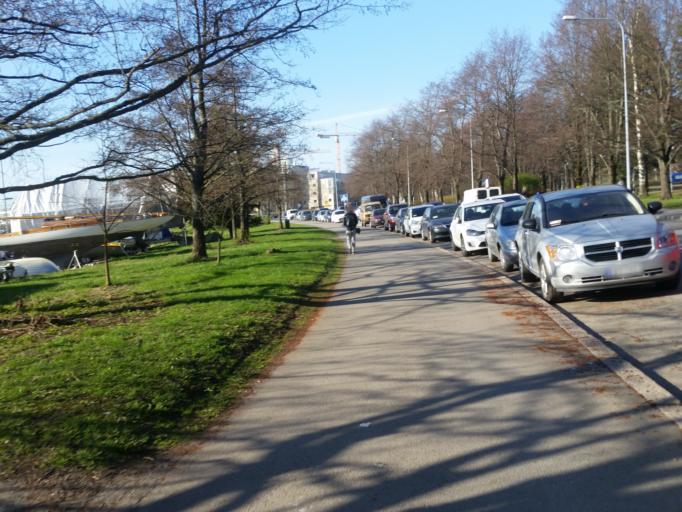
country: FI
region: Uusimaa
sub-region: Helsinki
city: Helsinki
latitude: 60.1588
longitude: 24.8869
